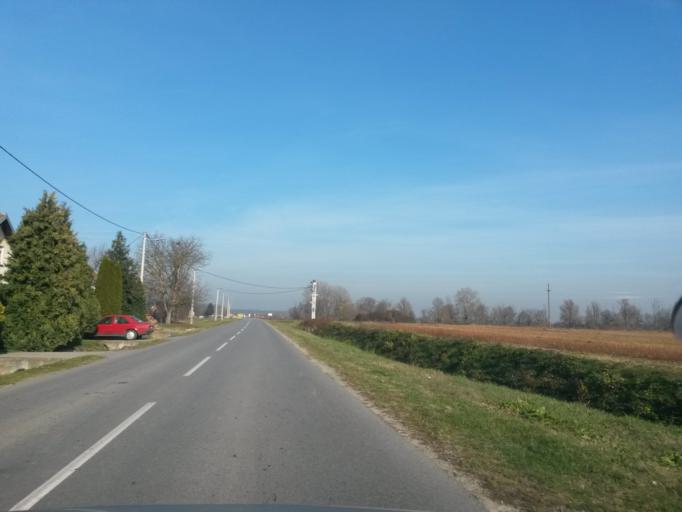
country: HR
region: Vukovarsko-Srijemska
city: Privlaka
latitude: 45.2090
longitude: 18.8551
